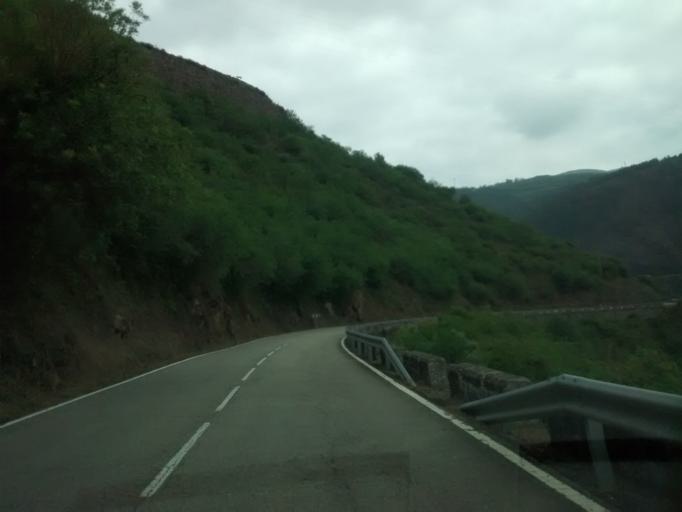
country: ES
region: Galicia
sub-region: Provincia de Ourense
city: Manzaneda
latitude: 42.3239
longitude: -7.2131
